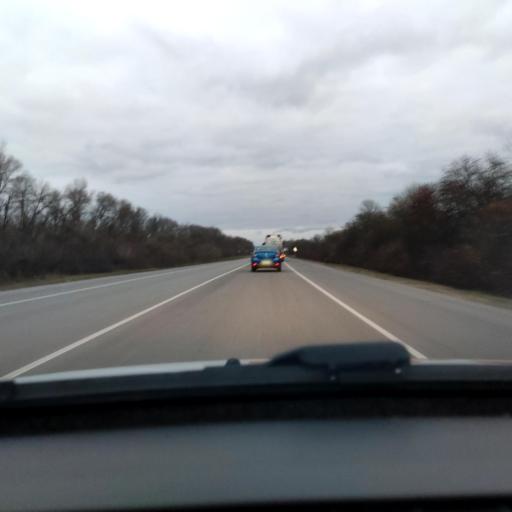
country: RU
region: Lipetsk
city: Borinskoye
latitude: 52.4557
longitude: 39.3054
